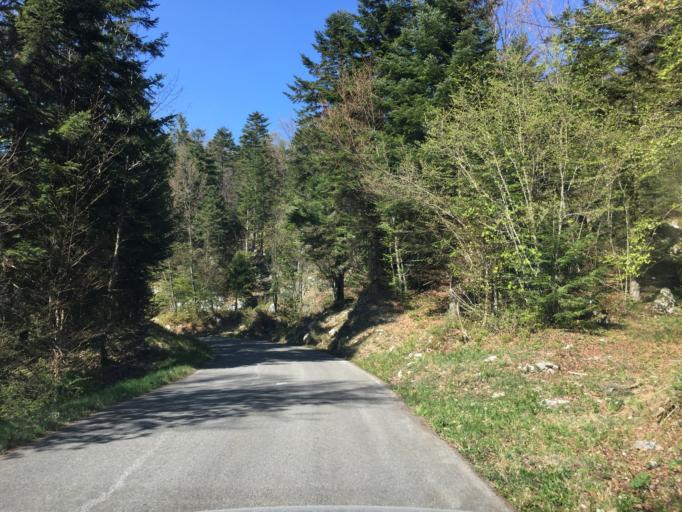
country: FR
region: Rhone-Alpes
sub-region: Departement de la Savoie
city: Novalaise
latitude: 45.5847
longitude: 5.8152
